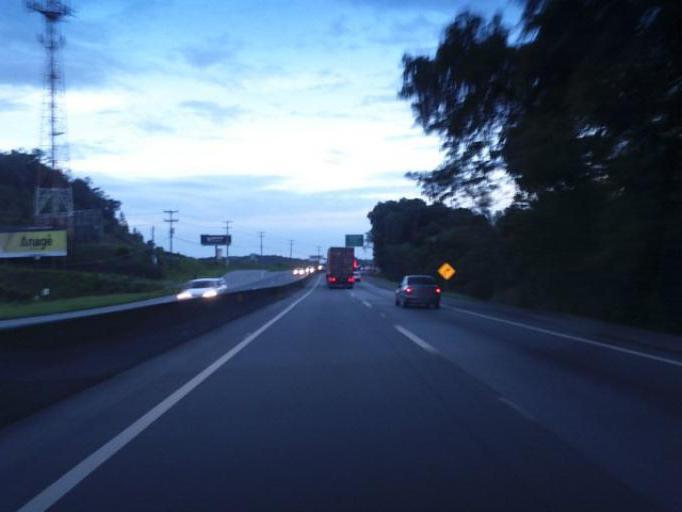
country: BR
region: Santa Catarina
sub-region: Joinville
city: Joinville
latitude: -26.2428
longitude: -48.9113
